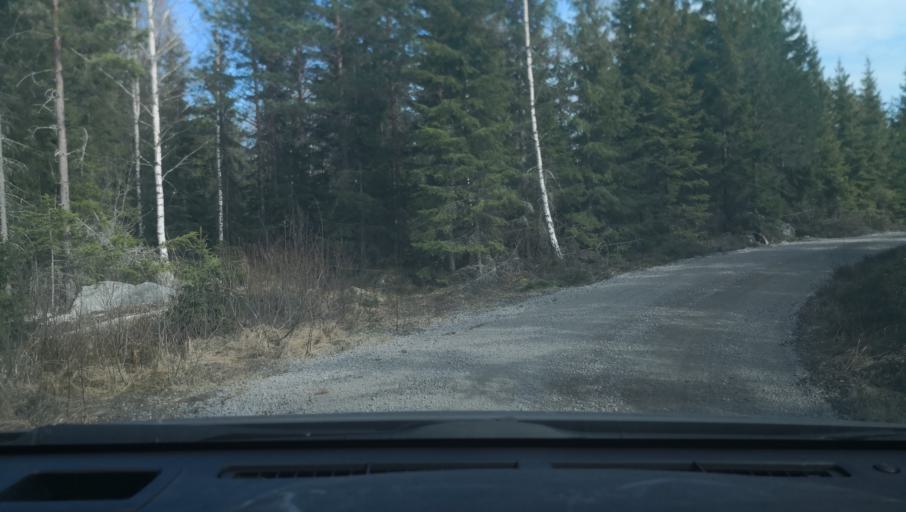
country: SE
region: Uppsala
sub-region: Heby Kommun
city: Heby
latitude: 59.8418
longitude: 16.8578
